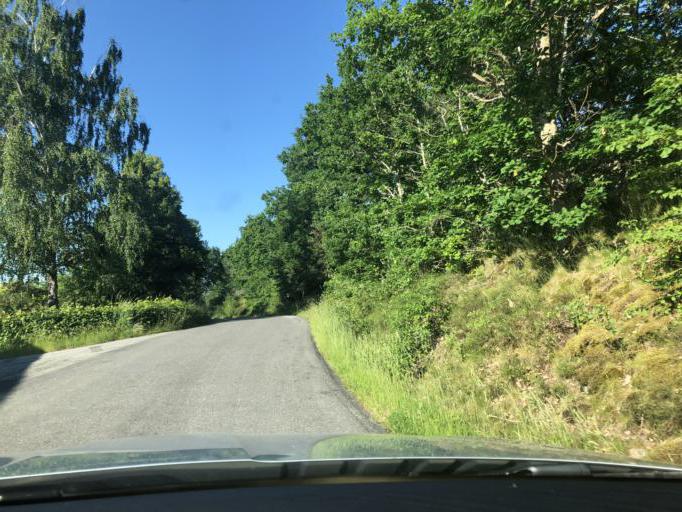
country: SE
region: Blekinge
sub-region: Karlshamns Kommun
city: Karlshamn
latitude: 56.1662
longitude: 14.8056
